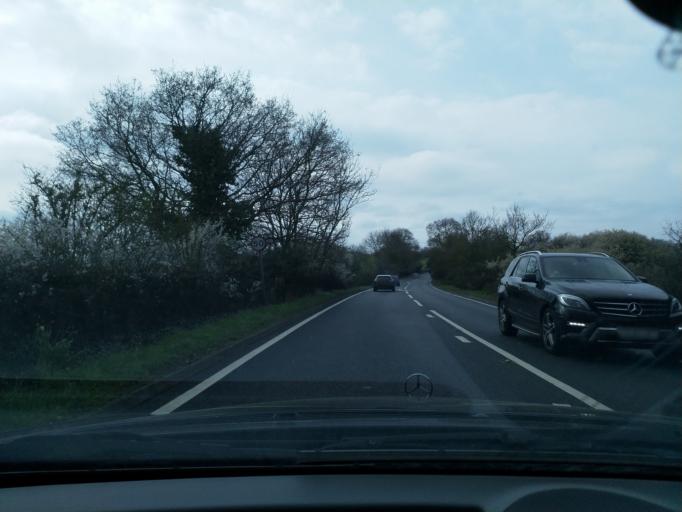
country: GB
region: England
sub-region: Warwickshire
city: Stratford-upon-Avon
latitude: 52.2210
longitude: -1.6675
